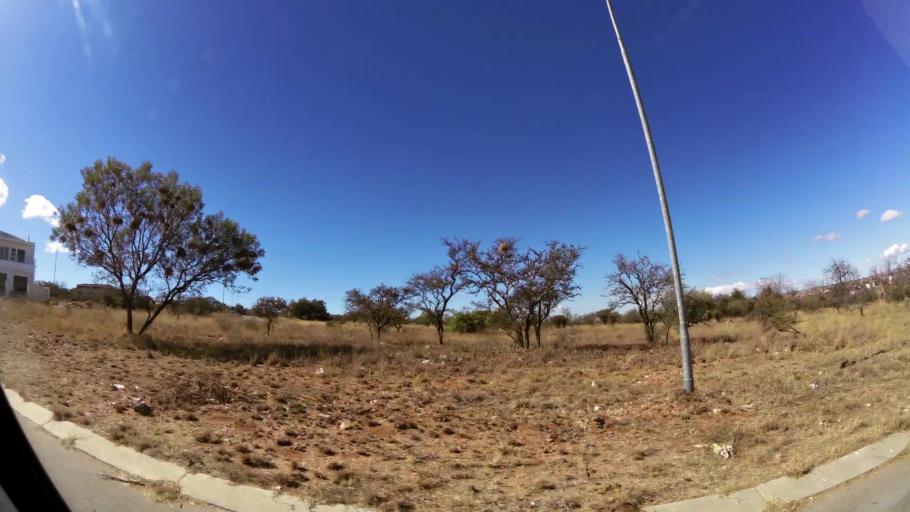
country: ZA
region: Limpopo
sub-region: Capricorn District Municipality
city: Polokwane
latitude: -23.8986
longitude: 29.4904
